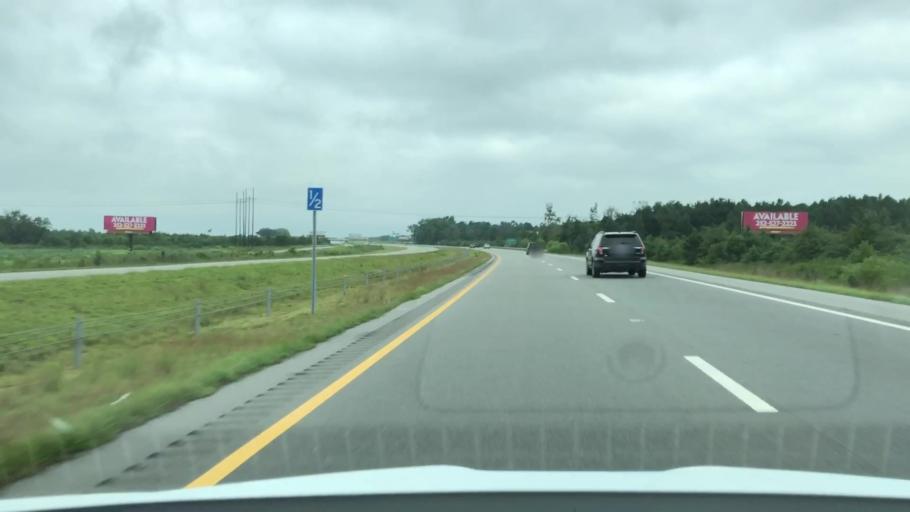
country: US
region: North Carolina
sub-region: Wayne County
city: Elroy
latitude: 35.3970
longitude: -77.8698
